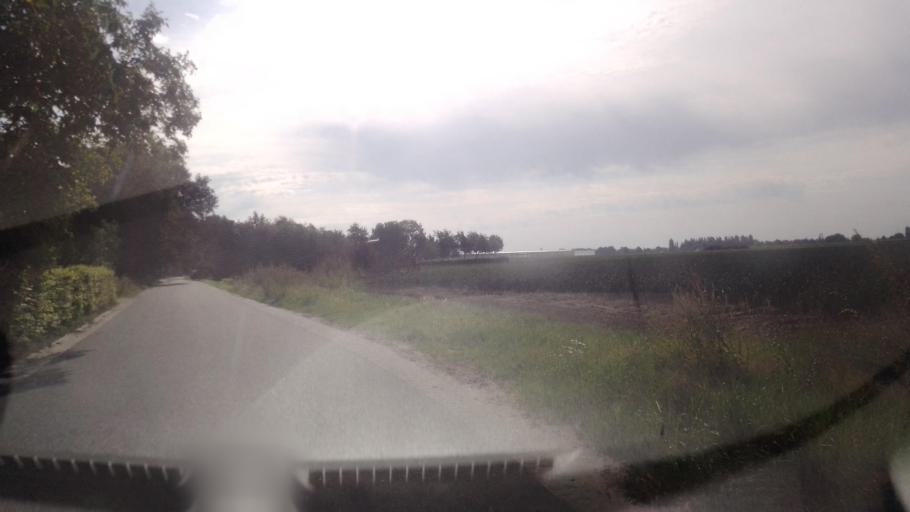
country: NL
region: Limburg
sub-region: Gemeente Venray
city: Venray
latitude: 51.4663
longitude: 6.0243
